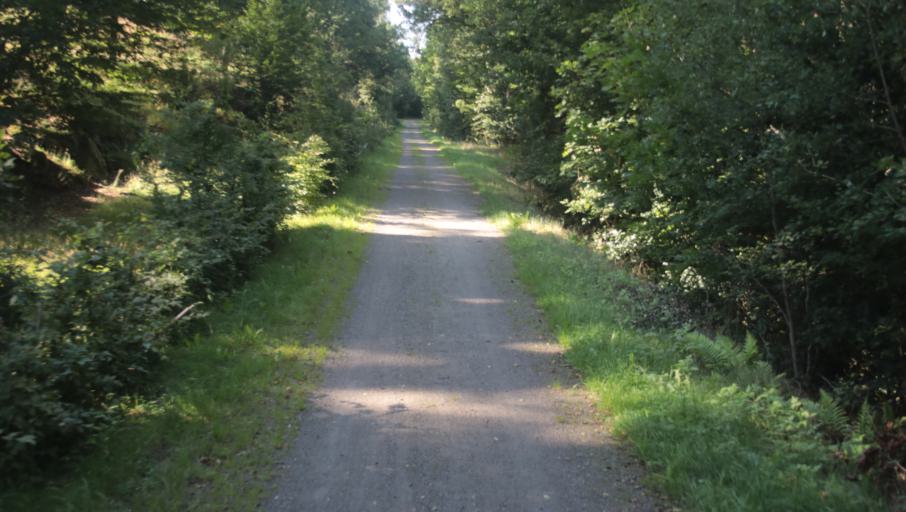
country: SE
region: Blekinge
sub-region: Karlshamns Kommun
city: Svangsta
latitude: 56.2802
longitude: 14.7558
